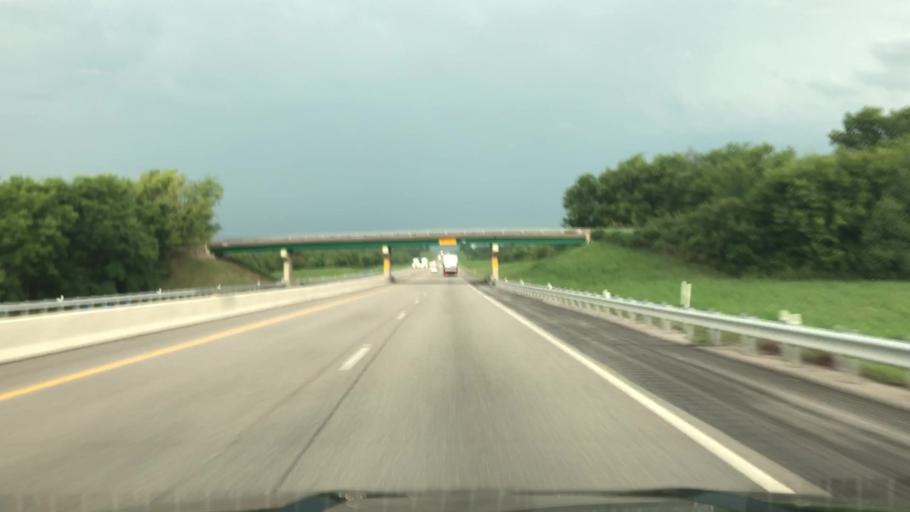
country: US
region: Oklahoma
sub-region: Rogers County
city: Justice
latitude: 36.3306
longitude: -95.5247
